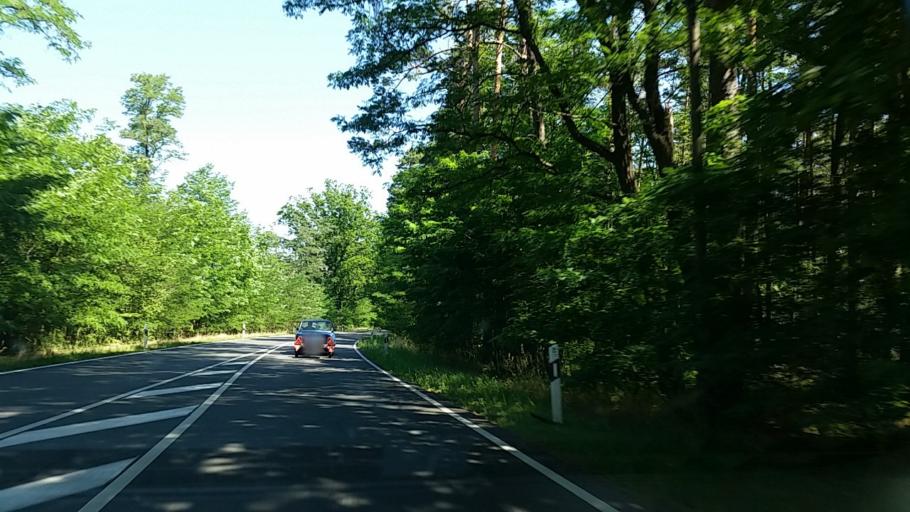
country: DE
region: Saxony-Anhalt
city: Kemberg
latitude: 51.7303
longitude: 12.6165
